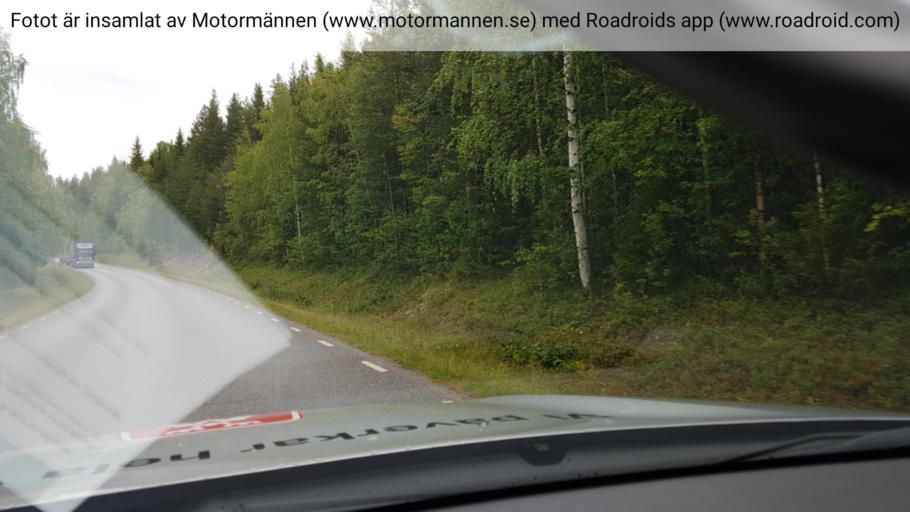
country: SE
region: Norrbotten
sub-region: Gallivare Kommun
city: Gaellivare
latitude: 66.4455
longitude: 20.6513
